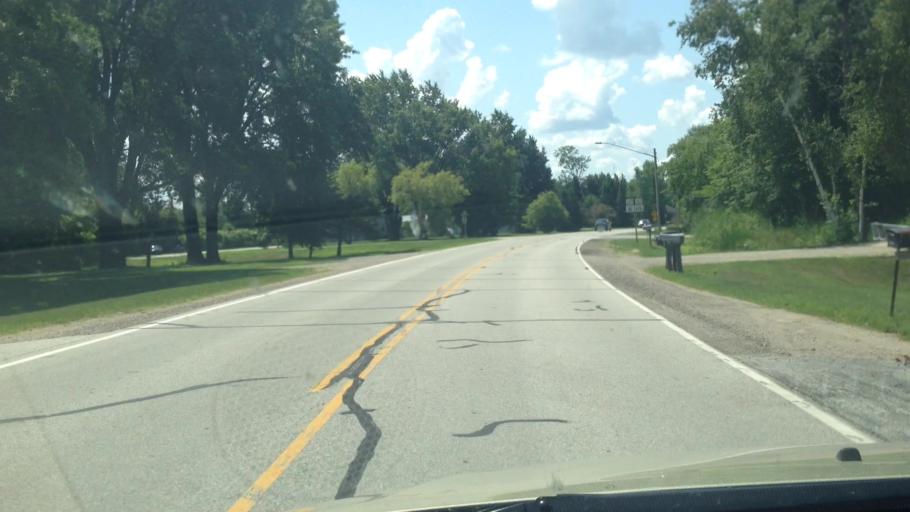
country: US
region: Wisconsin
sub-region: Brown County
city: Suamico
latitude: 44.6375
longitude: -88.0498
